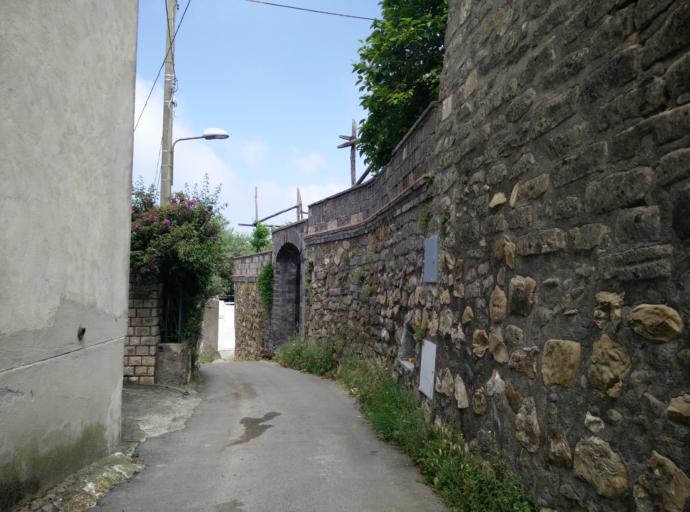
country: IT
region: Campania
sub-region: Provincia di Napoli
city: Massa Lubrense
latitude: 40.5987
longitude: 14.3840
